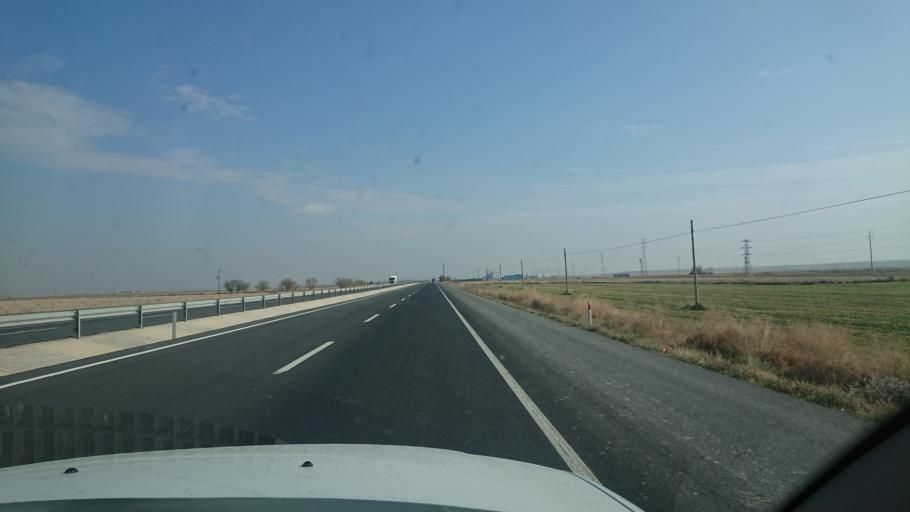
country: TR
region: Aksaray
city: Yesilova
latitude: 38.3151
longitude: 33.8479
